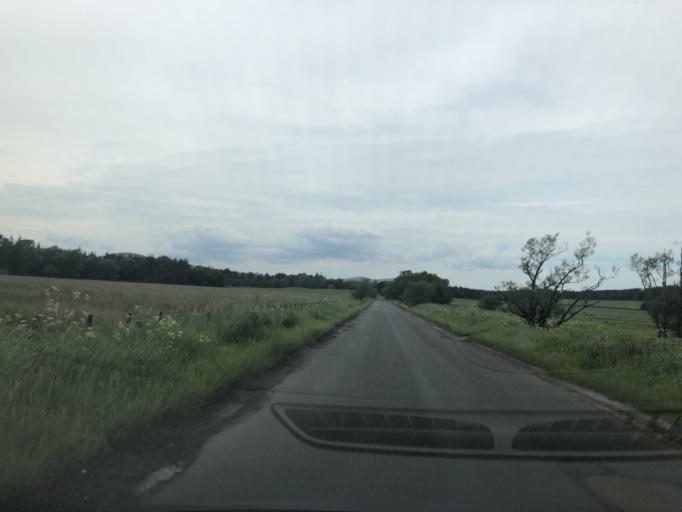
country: GB
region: Scotland
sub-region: The Scottish Borders
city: West Linton
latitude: 55.7292
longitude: -3.3206
